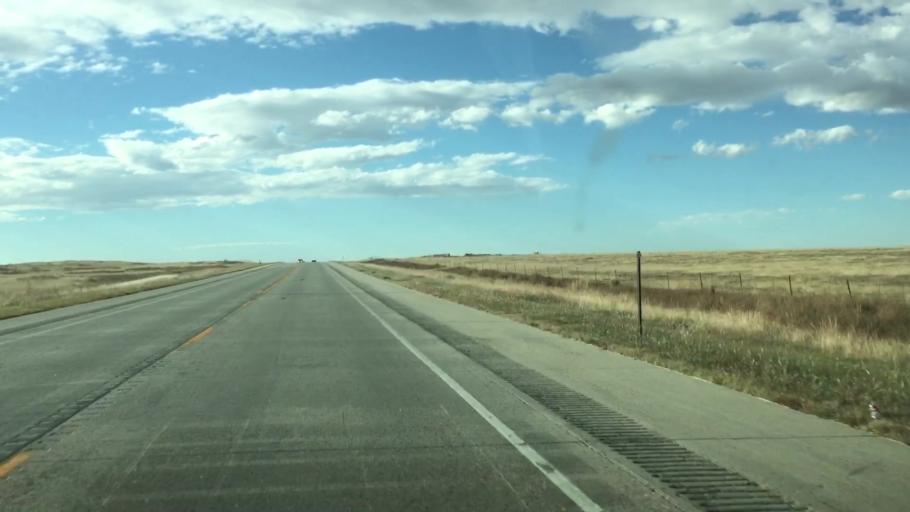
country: US
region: Colorado
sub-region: Lincoln County
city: Hugo
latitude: 39.1735
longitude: -103.5358
